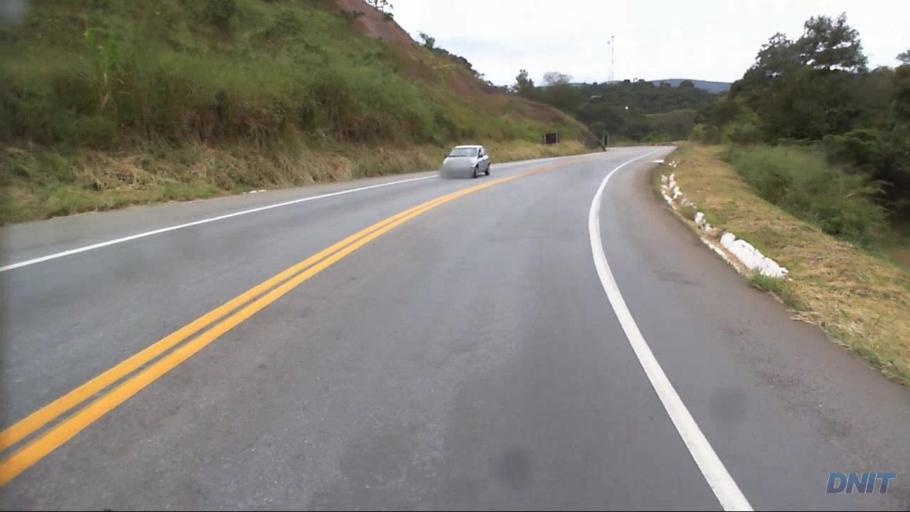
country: BR
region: Minas Gerais
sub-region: Joao Monlevade
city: Joao Monlevade
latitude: -19.8587
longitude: -43.2347
